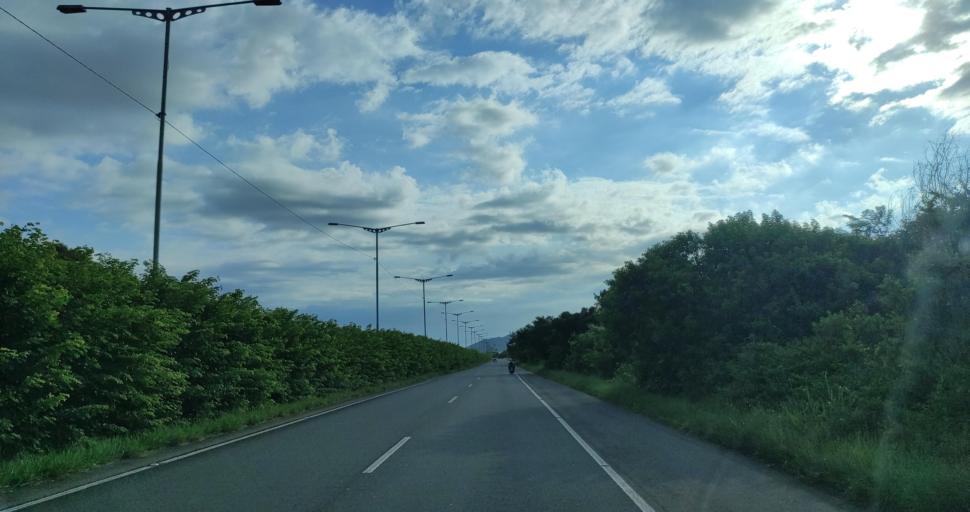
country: BR
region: Santa Catarina
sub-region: Penha
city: Penha
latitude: -26.8053
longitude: -48.6376
